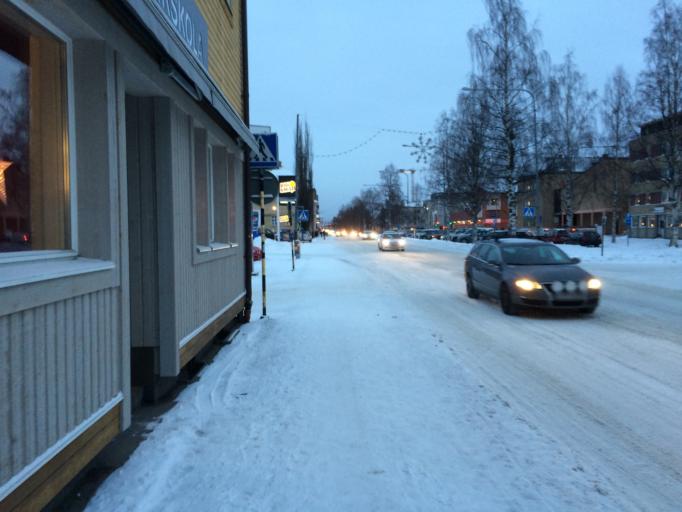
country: SE
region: Vaesterbotten
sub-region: Skelleftea Kommun
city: Skelleftea
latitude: 64.7523
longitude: 20.9484
